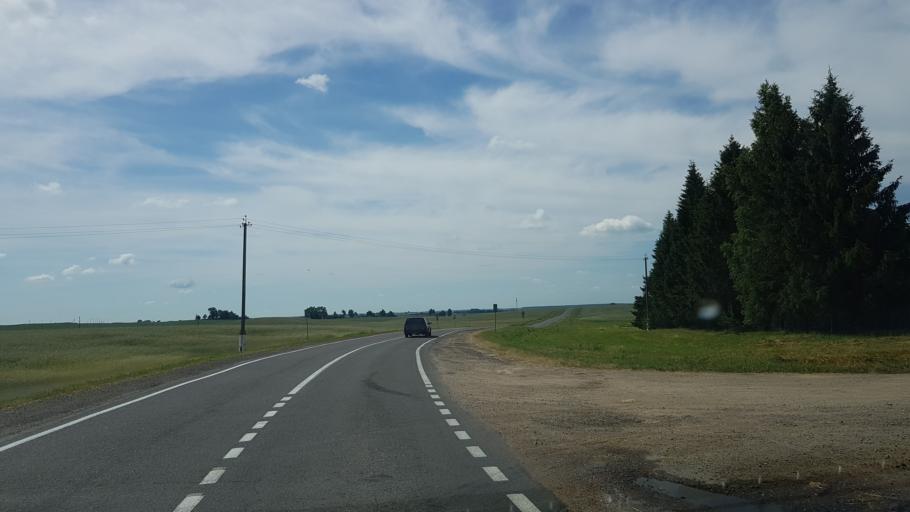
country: BY
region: Vitebsk
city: Dubrowna
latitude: 54.6510
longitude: 30.6663
